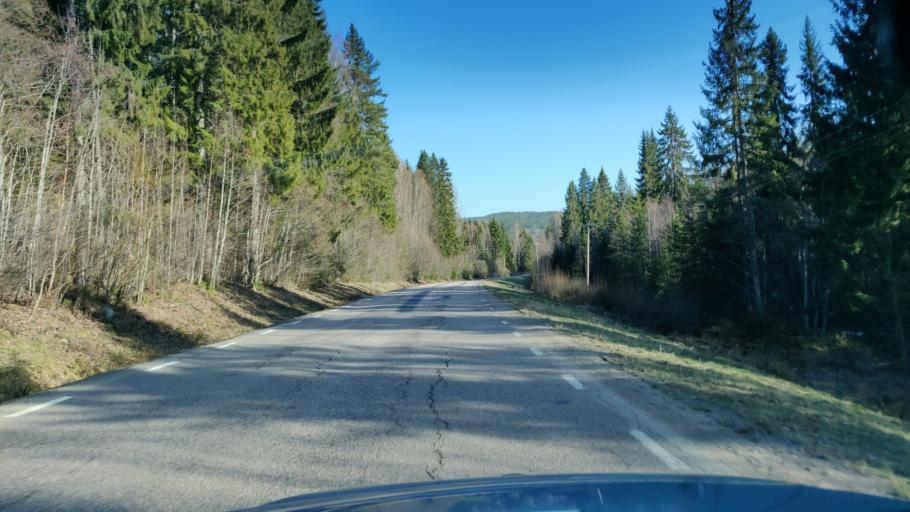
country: SE
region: Vaermland
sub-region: Munkfors Kommun
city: Munkfors
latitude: 59.9806
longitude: 13.4105
